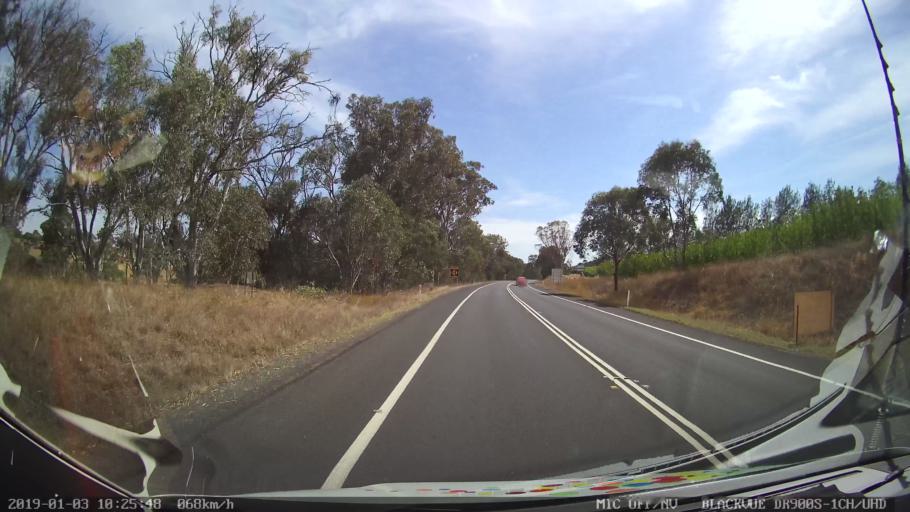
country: AU
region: New South Wales
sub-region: Young
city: Young
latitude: -34.4195
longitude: 148.2447
